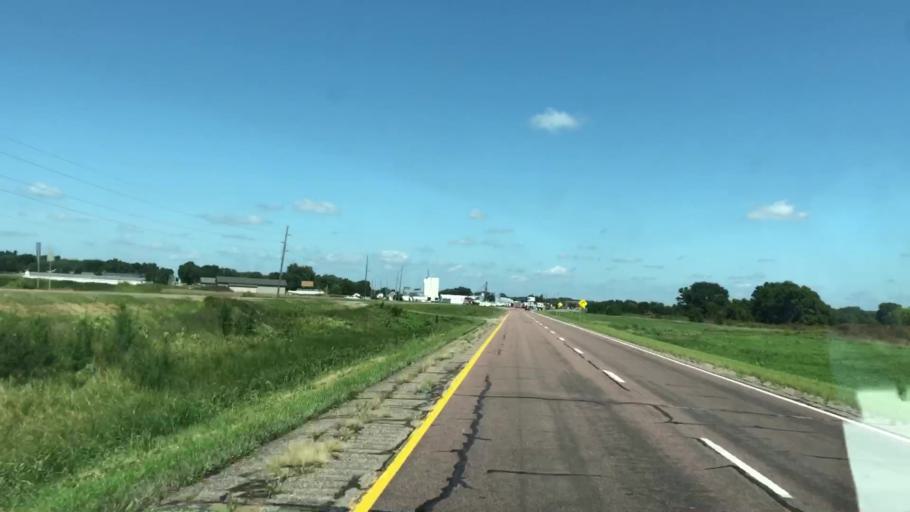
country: US
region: Iowa
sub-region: Plymouth County
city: Le Mars
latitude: 42.7097
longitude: -96.2526
